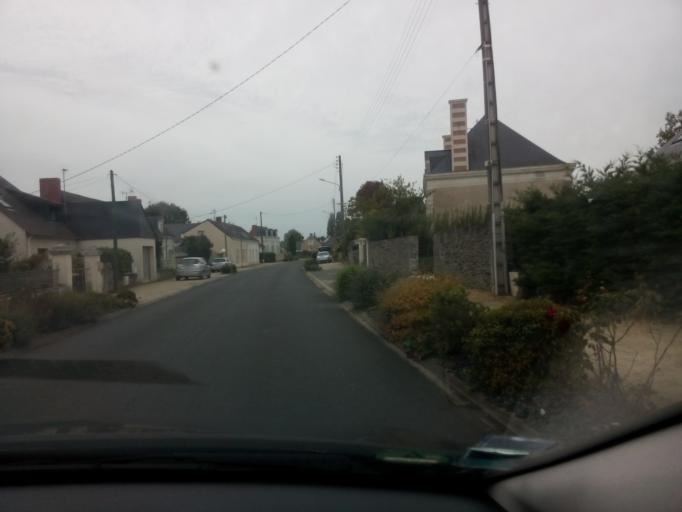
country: FR
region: Pays de la Loire
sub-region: Departement de Maine-et-Loire
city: Corne
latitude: 47.4711
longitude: -0.3426
